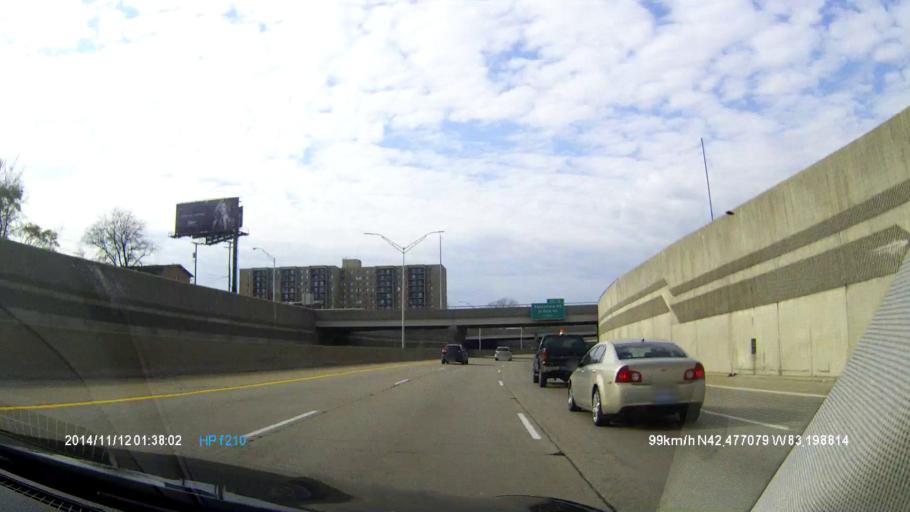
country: US
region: Michigan
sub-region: Oakland County
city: Southfield
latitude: 42.4770
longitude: -83.1992
